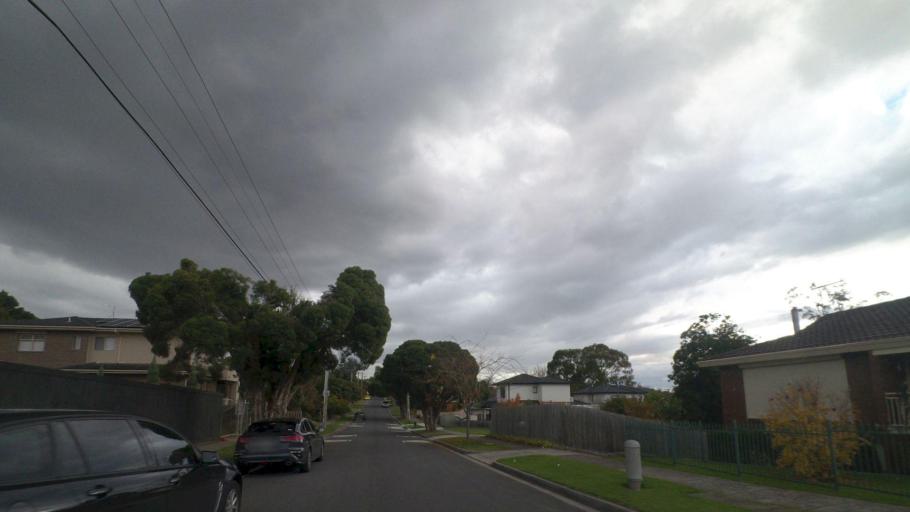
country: AU
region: Victoria
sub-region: Manningham
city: Doncaster East
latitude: -37.7877
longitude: 145.1582
